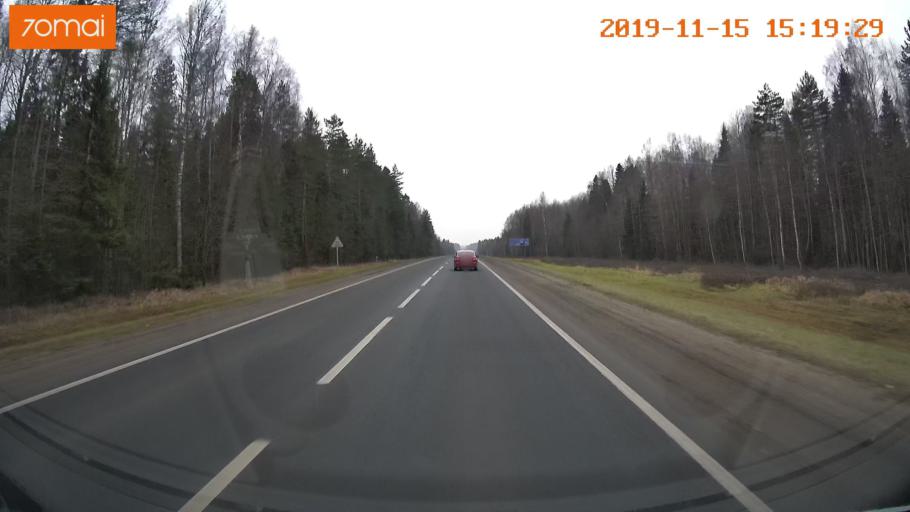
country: RU
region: Jaroslavl
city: Danilov
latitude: 58.2338
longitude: 40.1768
